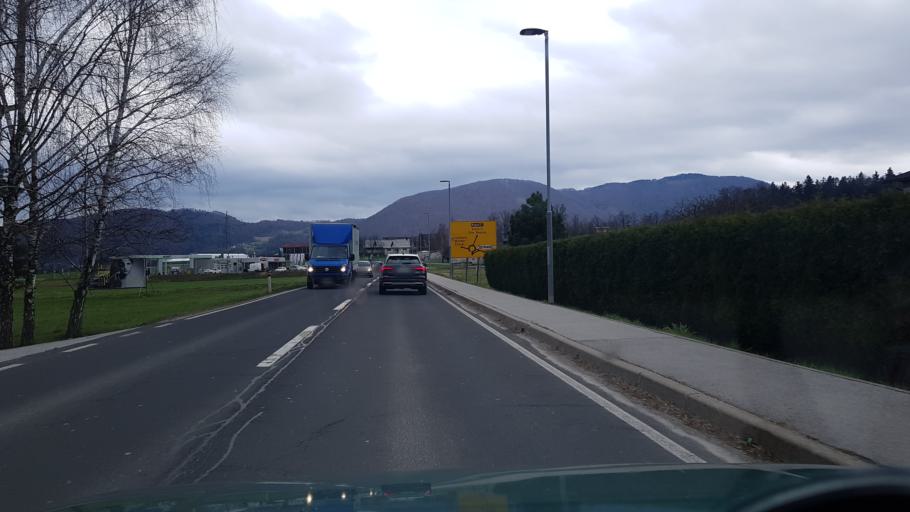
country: SI
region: Slovenska Konjice
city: Slovenske Konjice
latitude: 46.3426
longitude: 15.4711
